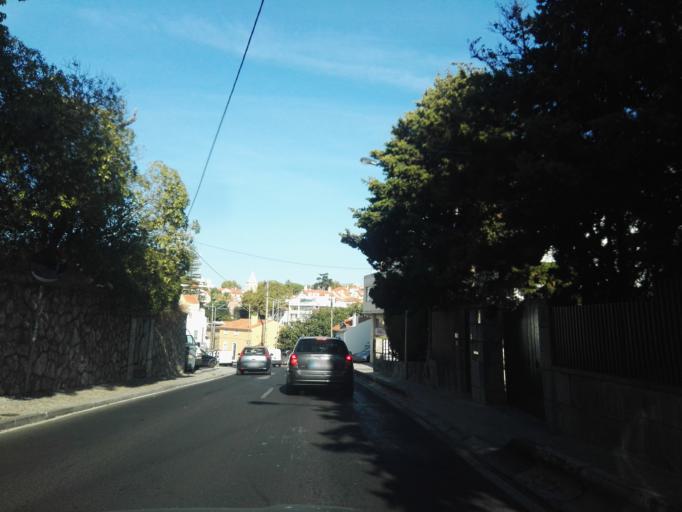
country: PT
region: Lisbon
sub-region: Cascais
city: Estoril
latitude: 38.7025
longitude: -9.3901
